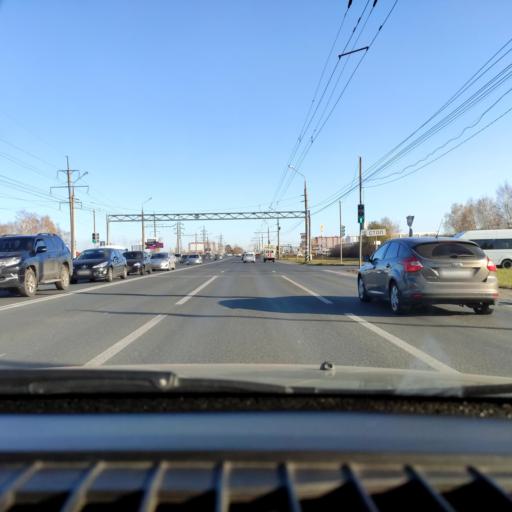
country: RU
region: Samara
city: Tol'yatti
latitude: 53.5465
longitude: 49.3727
